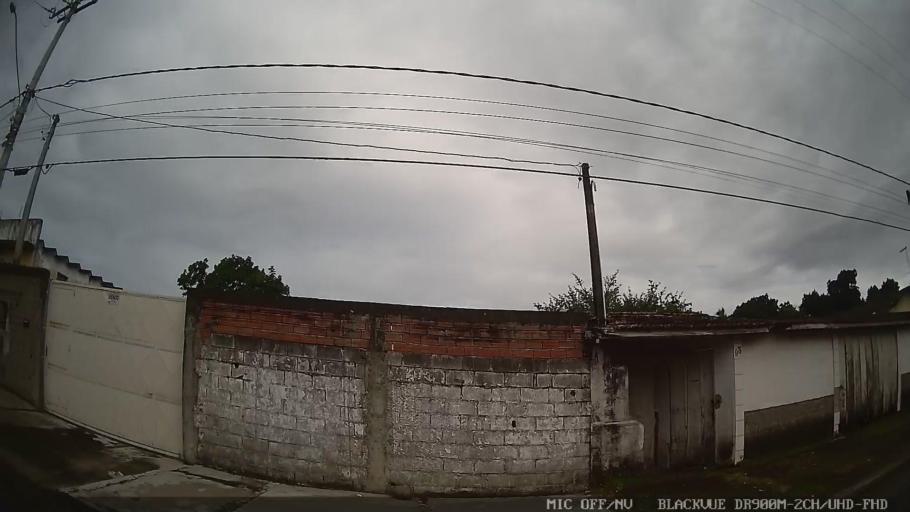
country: BR
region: Sao Paulo
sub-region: Itanhaem
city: Itanhaem
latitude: -24.1642
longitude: -46.7875
